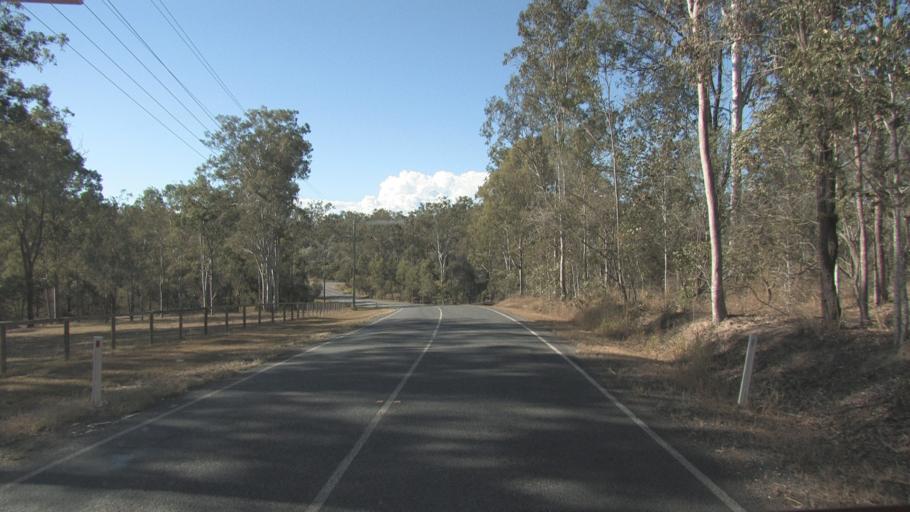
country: AU
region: Queensland
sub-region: Logan
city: Cedar Vale
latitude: -27.8349
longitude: 153.0513
